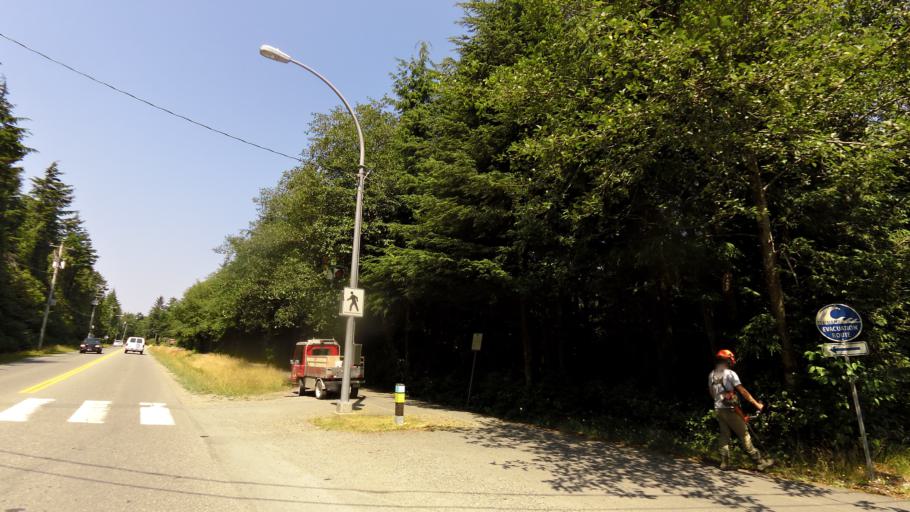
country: CA
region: British Columbia
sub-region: Regional District of Alberni-Clayoquot
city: Tofino
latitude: 49.1235
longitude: -125.8917
